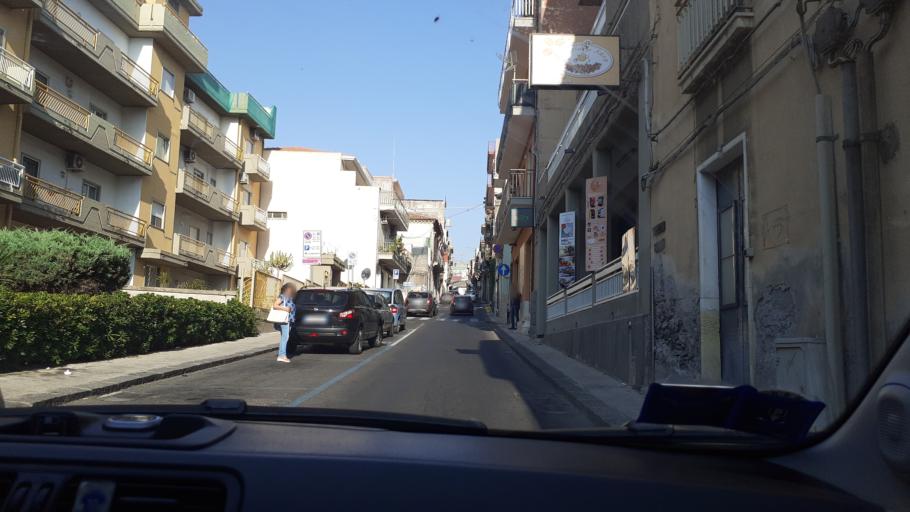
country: IT
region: Sicily
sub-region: Catania
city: Misterbianco
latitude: 37.5176
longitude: 15.0116
